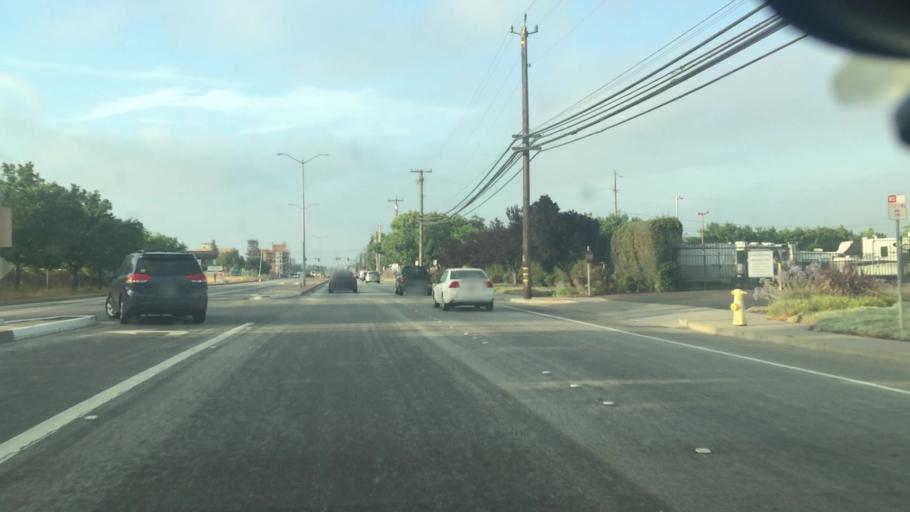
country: US
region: California
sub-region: Alameda County
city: Fremont
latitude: 37.5057
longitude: -121.9494
